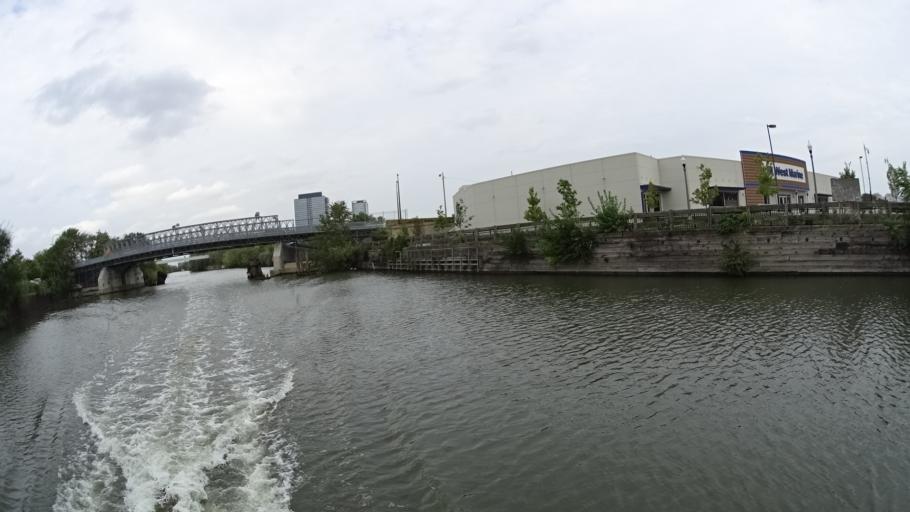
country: US
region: Illinois
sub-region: Cook County
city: Chicago
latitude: 41.9030
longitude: -87.6491
